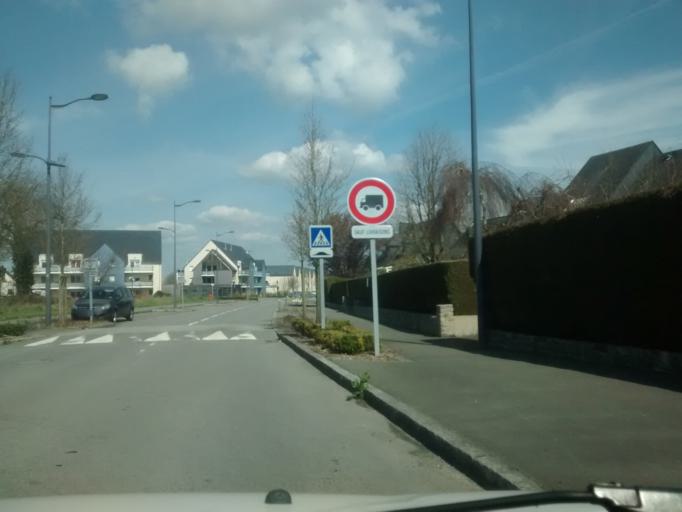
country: FR
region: Brittany
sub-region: Departement d'Ille-et-Vilaine
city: Brece
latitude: 48.1066
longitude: -1.4860
